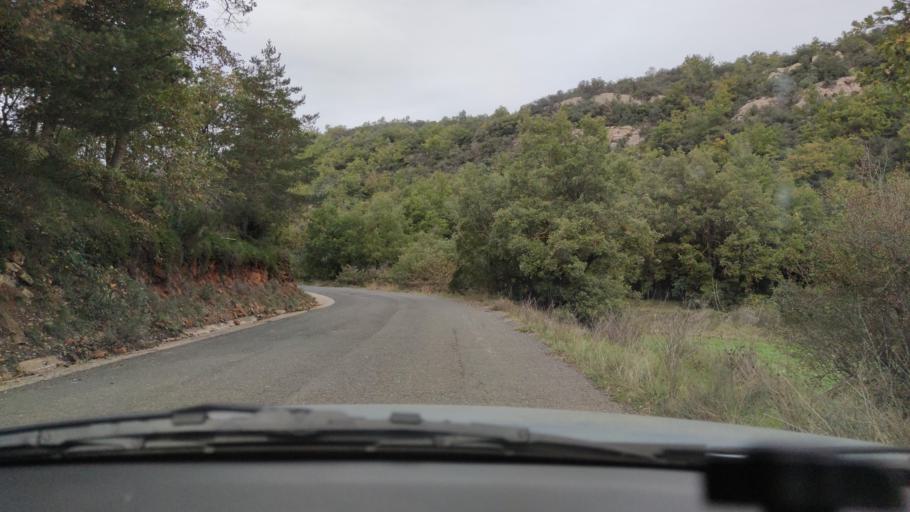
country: ES
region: Catalonia
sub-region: Provincia de Lleida
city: Llimiana
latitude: 42.0372
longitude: 1.0186
